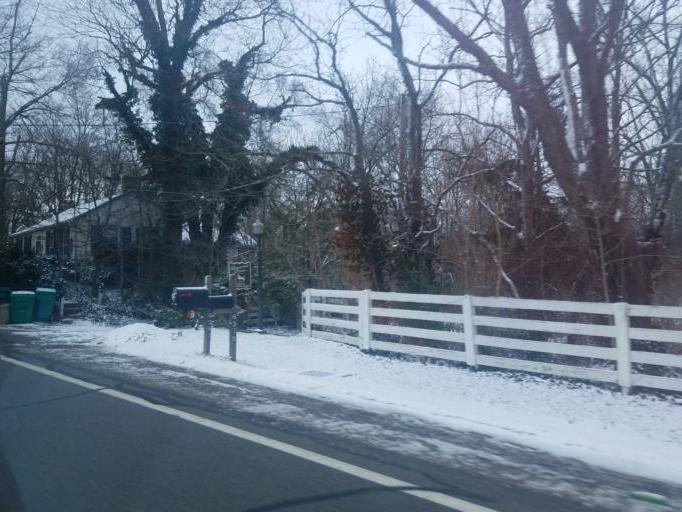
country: US
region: Ohio
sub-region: Franklin County
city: New Albany
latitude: 40.0420
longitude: -82.8231
